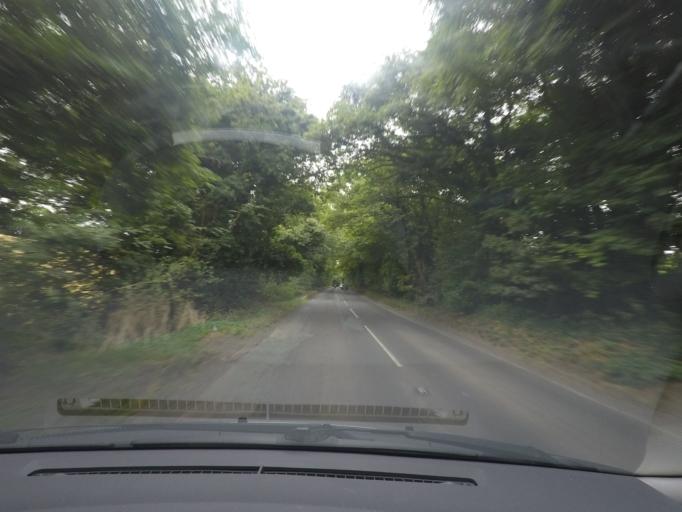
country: GB
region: England
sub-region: Wiltshire
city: Marlborough
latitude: 51.4029
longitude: -1.7454
